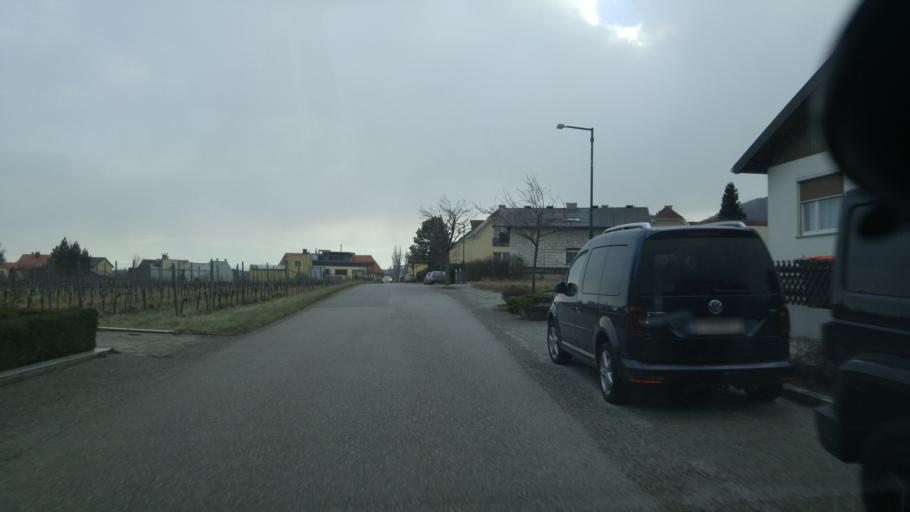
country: AT
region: Lower Austria
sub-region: Politischer Bezirk Baden
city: Bad Voslau
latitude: 47.9866
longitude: 16.2082
